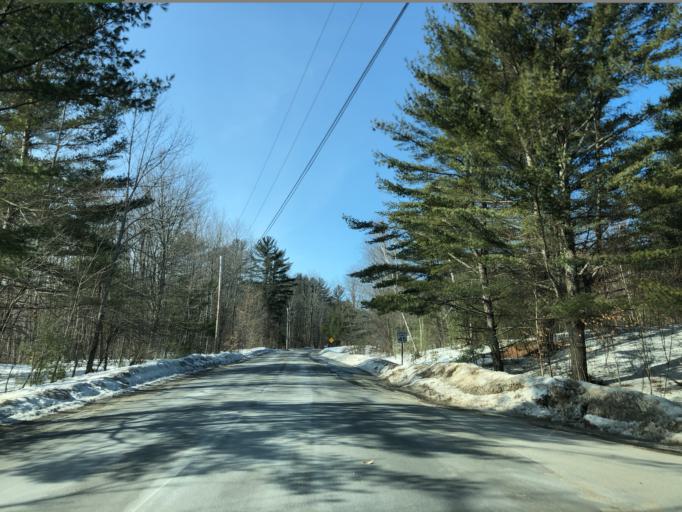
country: US
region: Maine
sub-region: Androscoggin County
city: Minot
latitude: 44.1418
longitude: -70.3211
